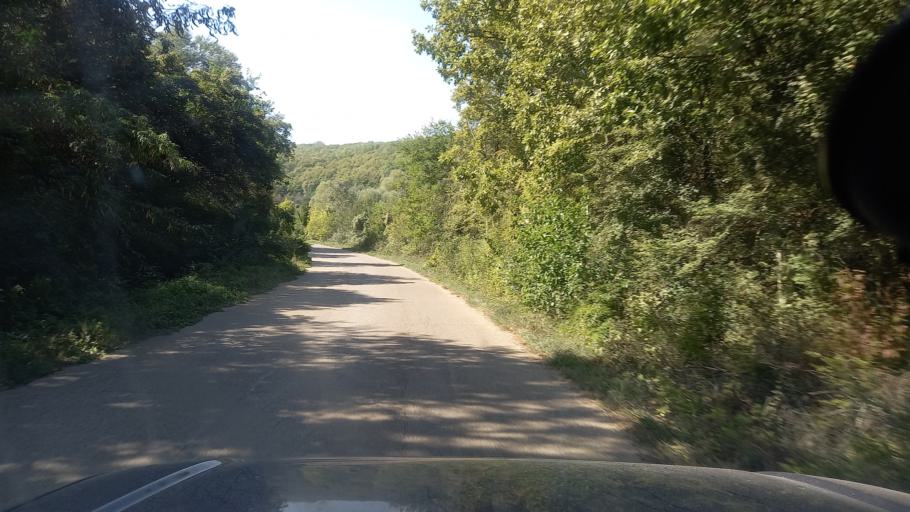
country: RU
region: Krasnodarskiy
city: Azovskaya
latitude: 44.7100
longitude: 38.6758
